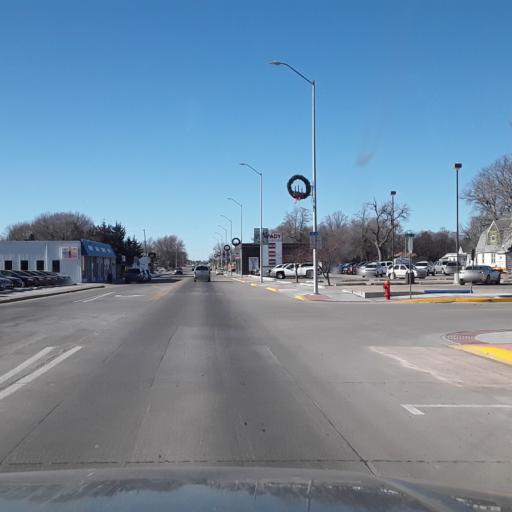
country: US
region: Nebraska
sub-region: Phelps County
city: Holdrege
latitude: 40.4380
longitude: -99.3721
